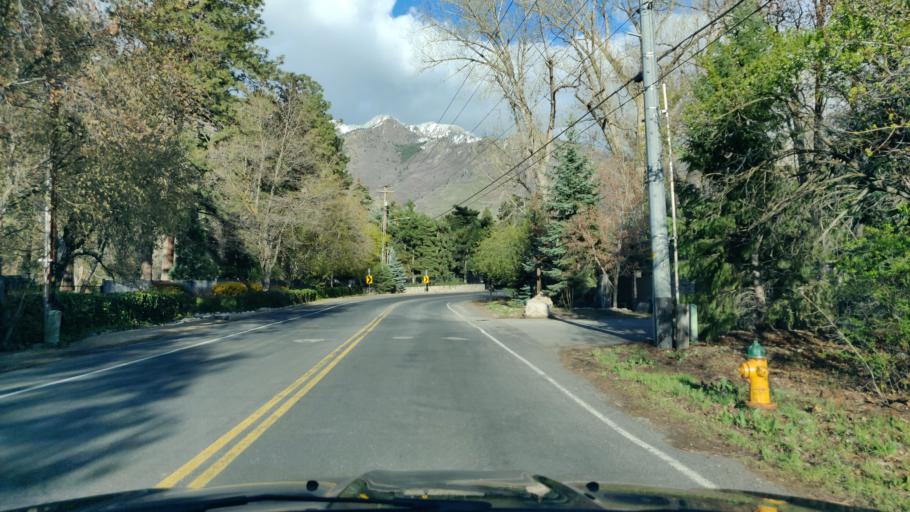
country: US
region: Utah
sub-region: Salt Lake County
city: Cottonwood Heights
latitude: 40.6385
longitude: -111.8155
